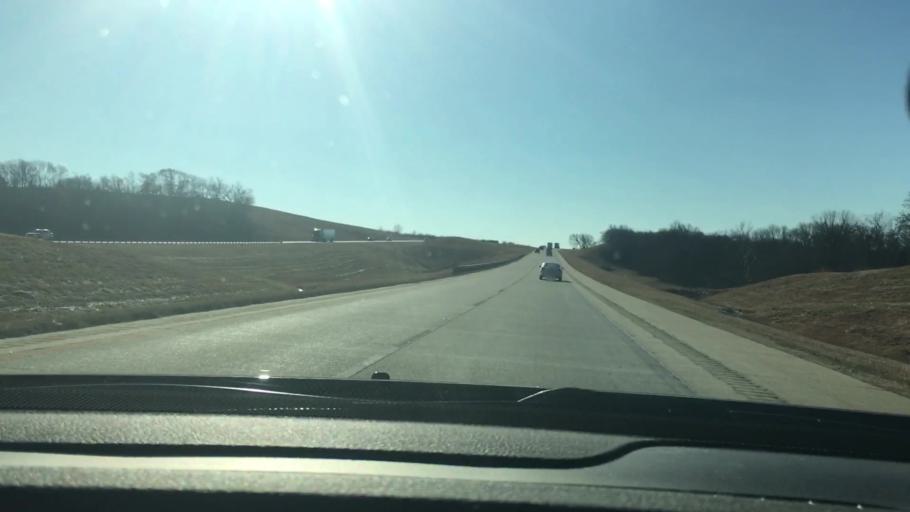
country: US
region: Oklahoma
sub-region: Love County
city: Marietta
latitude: 33.9875
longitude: -97.1382
